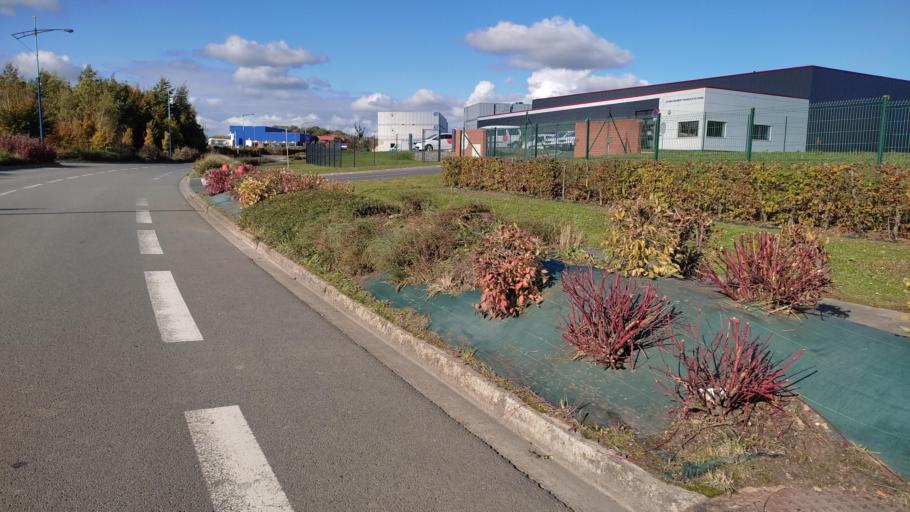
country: FR
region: Nord-Pas-de-Calais
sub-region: Departement du Pas-de-Calais
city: Saint-Laurent-Blangy
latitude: 50.3132
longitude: 2.8231
